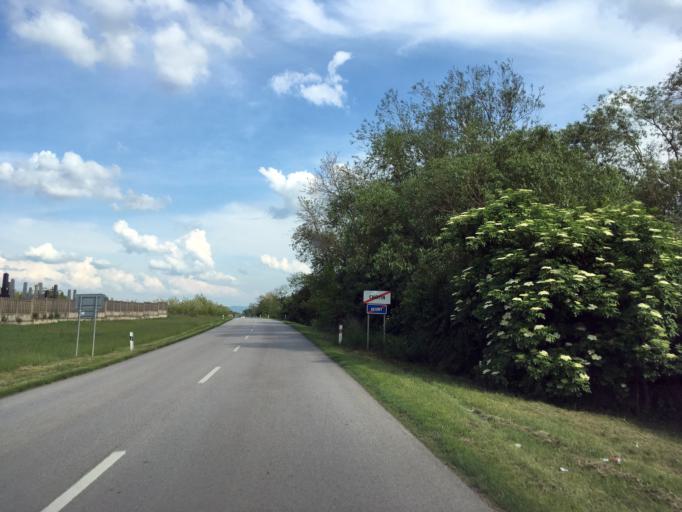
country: HU
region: Komarom-Esztergom
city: Almasfuzito
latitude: 47.7999
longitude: 18.2404
